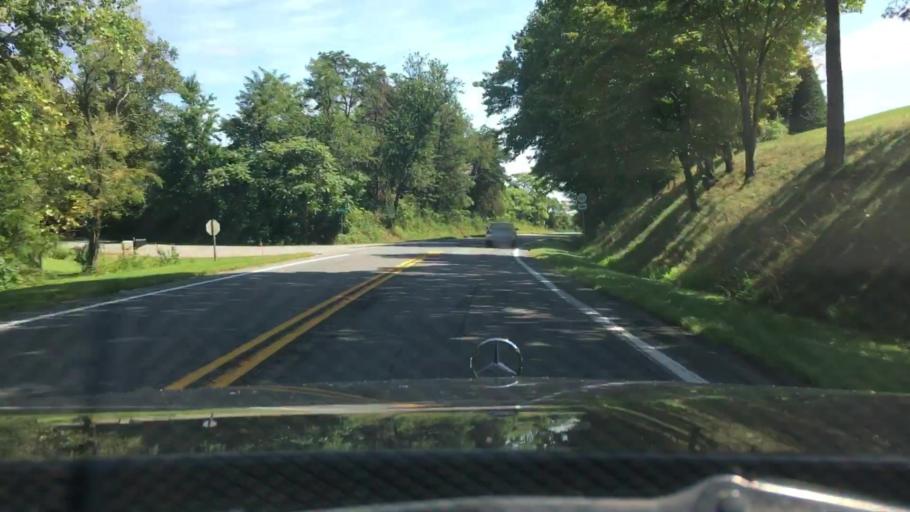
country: US
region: Virginia
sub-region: City of Waynesboro
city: Waynesboro
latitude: 38.0252
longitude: -78.8137
